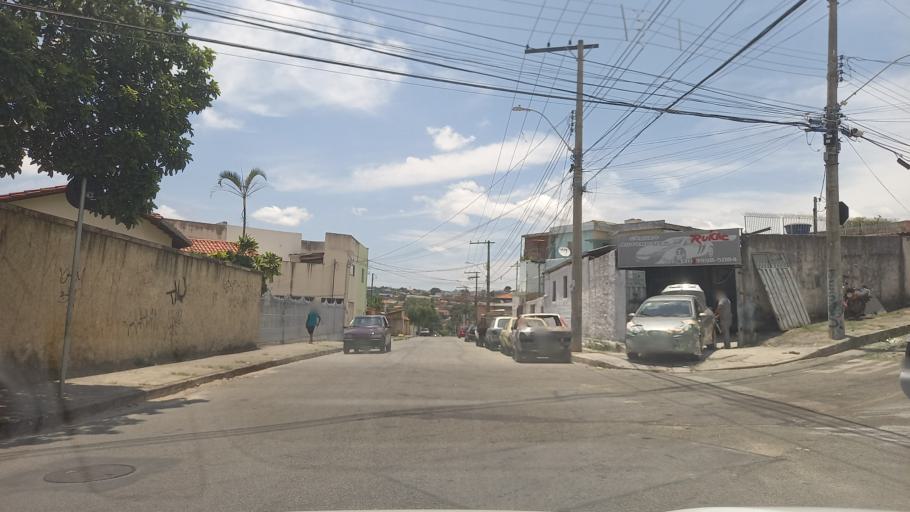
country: BR
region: Minas Gerais
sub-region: Contagem
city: Contagem
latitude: -19.9099
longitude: -44.0053
